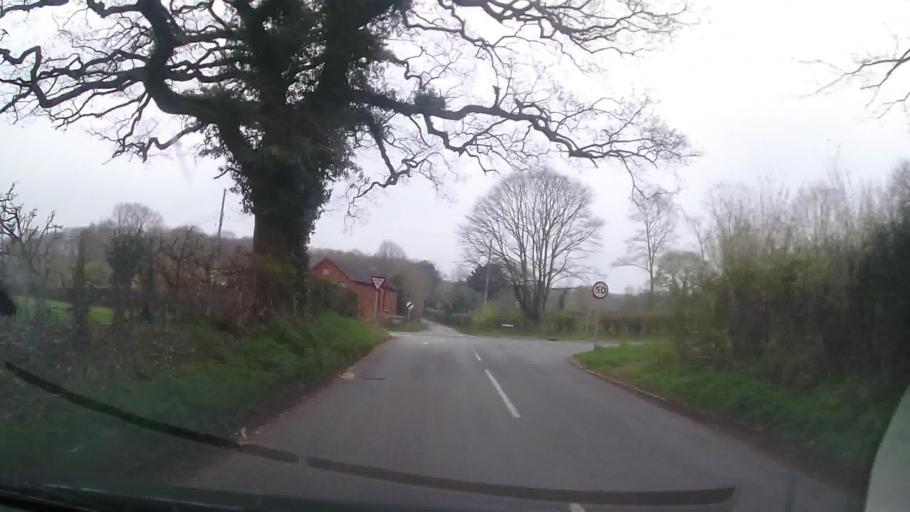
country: GB
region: England
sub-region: Staffordshire
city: Standon
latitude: 52.9477
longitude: -2.3509
